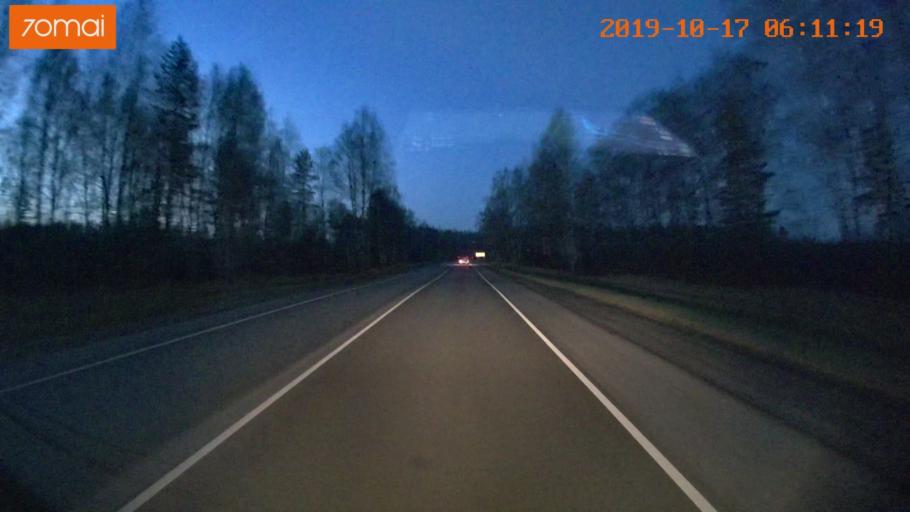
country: RU
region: Ivanovo
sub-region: Gorod Ivanovo
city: Ivanovo
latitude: 56.9206
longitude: 40.9584
